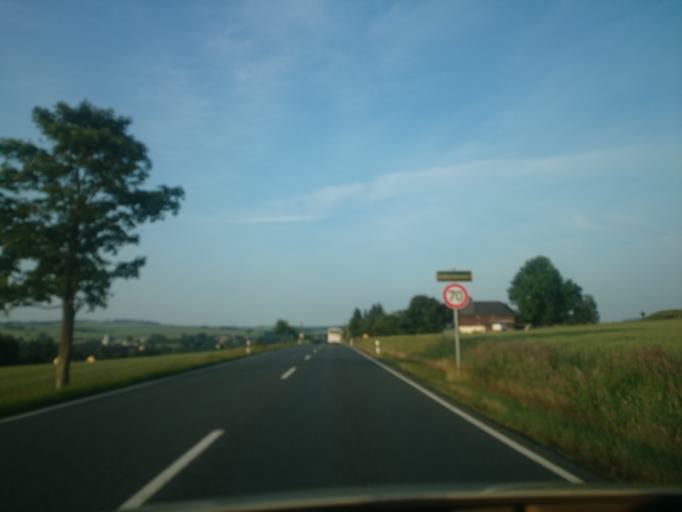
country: DE
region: Saxony
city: Grosshartmannsdorf
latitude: 50.8156
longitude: 13.3245
